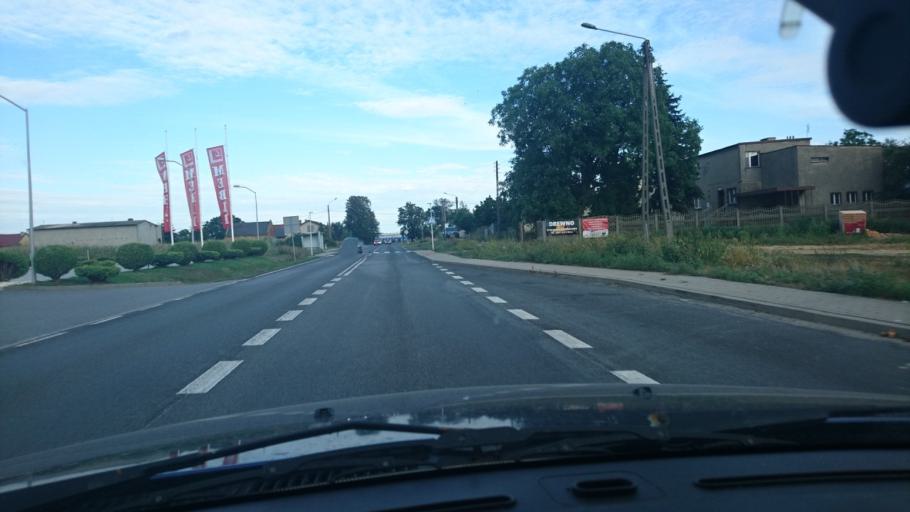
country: PL
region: Greater Poland Voivodeship
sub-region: Powiat kepinski
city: Slupia pod Kepnem
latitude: 51.2308
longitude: 18.0734
